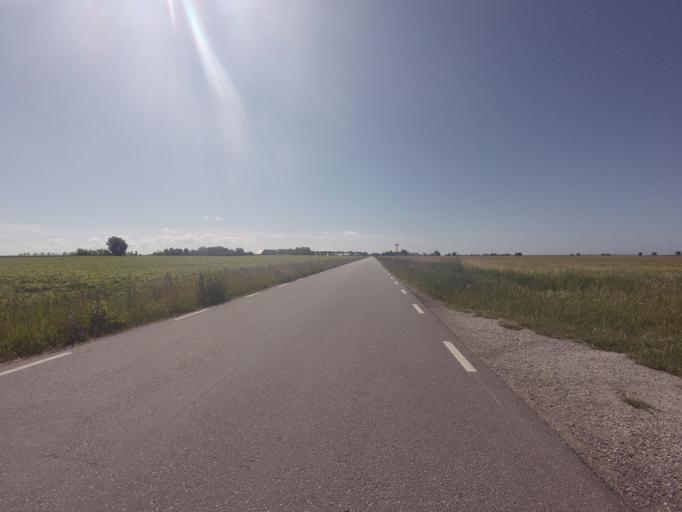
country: SE
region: Skane
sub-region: Malmo
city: Bunkeflostrand
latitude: 55.5190
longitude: 12.9338
